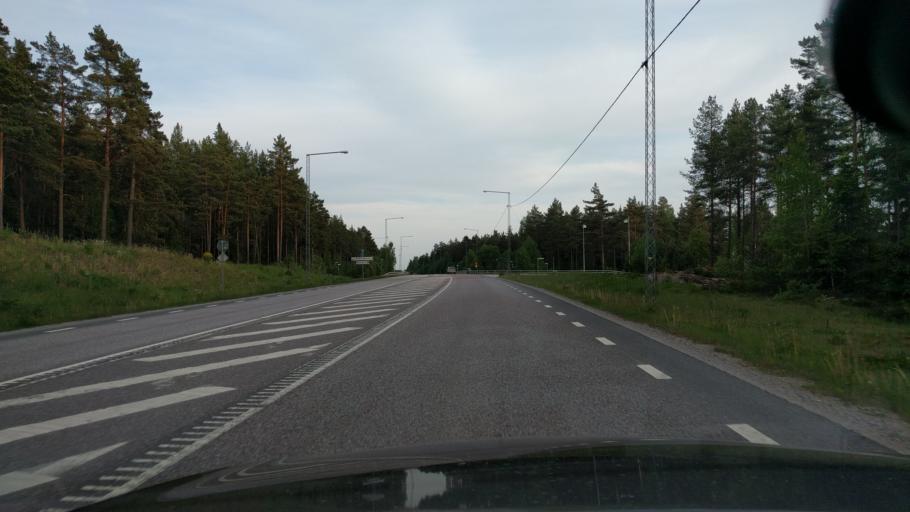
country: SE
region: Stockholm
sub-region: Vallentuna Kommun
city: Vallentuna
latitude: 59.5145
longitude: 18.0945
